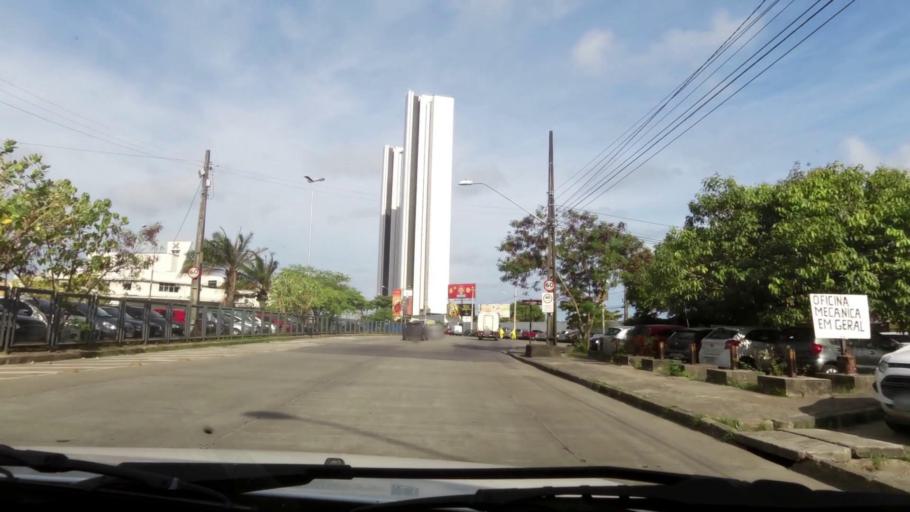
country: BR
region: Pernambuco
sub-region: Recife
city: Recife
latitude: -8.0713
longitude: -34.8769
